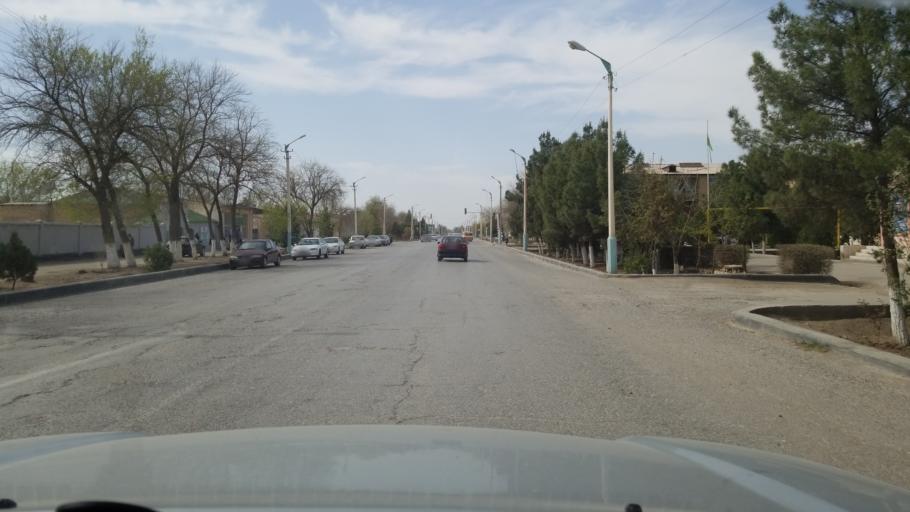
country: TM
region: Lebap
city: Atamyrat
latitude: 37.8382
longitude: 65.2121
